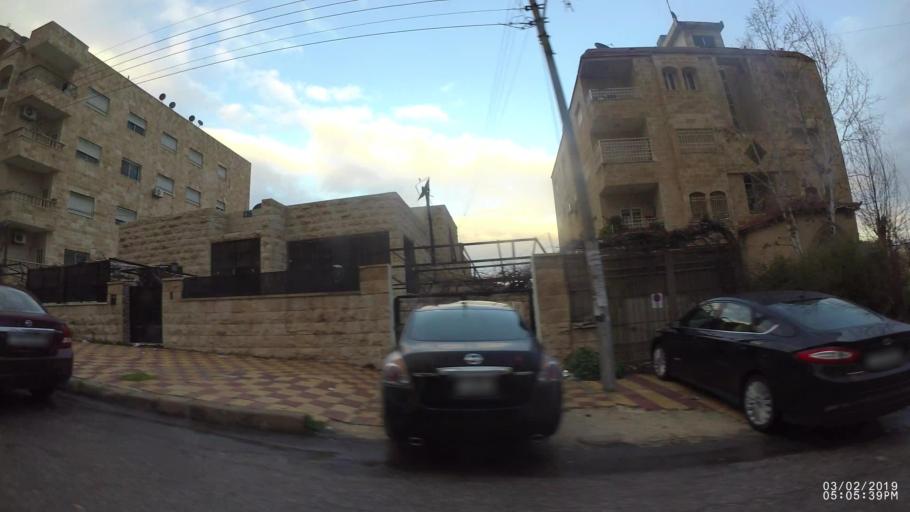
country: JO
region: Amman
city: Amman
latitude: 31.9859
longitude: 35.9159
